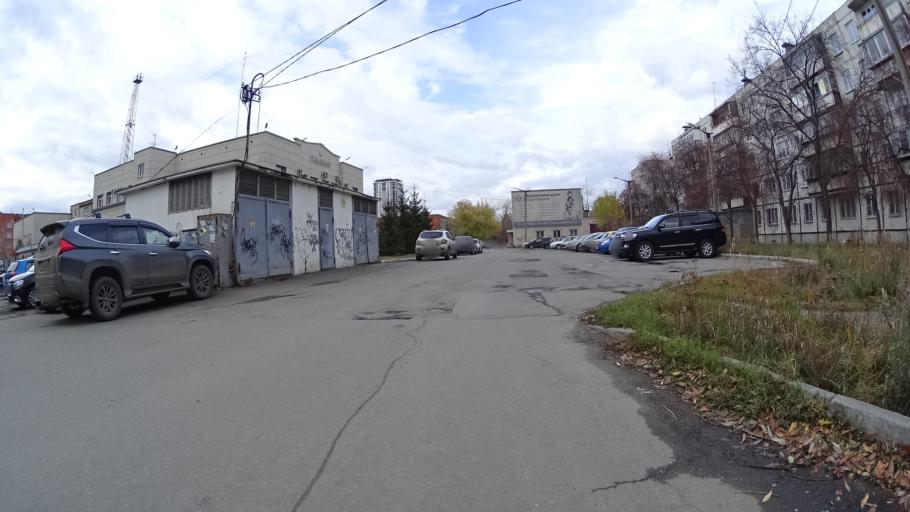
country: RU
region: Chelyabinsk
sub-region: Gorod Chelyabinsk
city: Chelyabinsk
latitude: 55.1907
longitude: 61.3114
